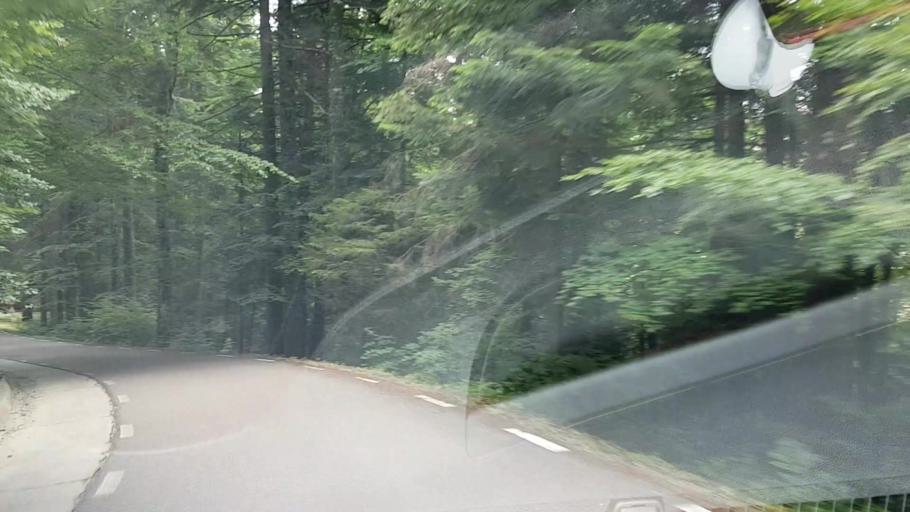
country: RO
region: Suceava
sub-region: Comuna Crucea
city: Crucea
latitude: 47.4329
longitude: 25.5735
